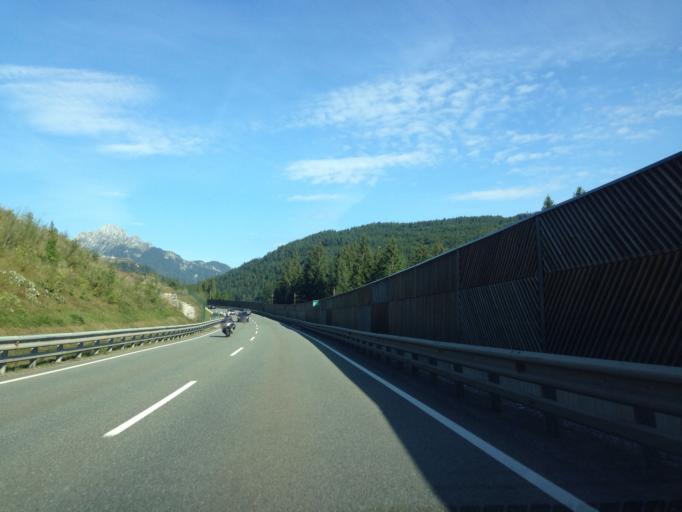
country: AT
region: Tyrol
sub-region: Politischer Bezirk Reutte
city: Heiterwang
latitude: 47.4455
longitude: 10.7389
